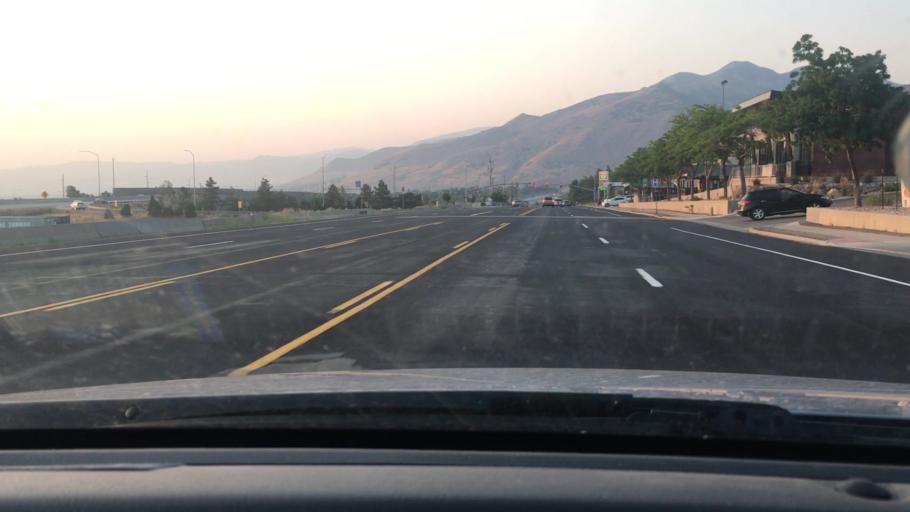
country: US
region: Utah
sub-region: Salt Lake County
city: Mount Olympus
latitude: 40.6846
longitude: -111.7960
